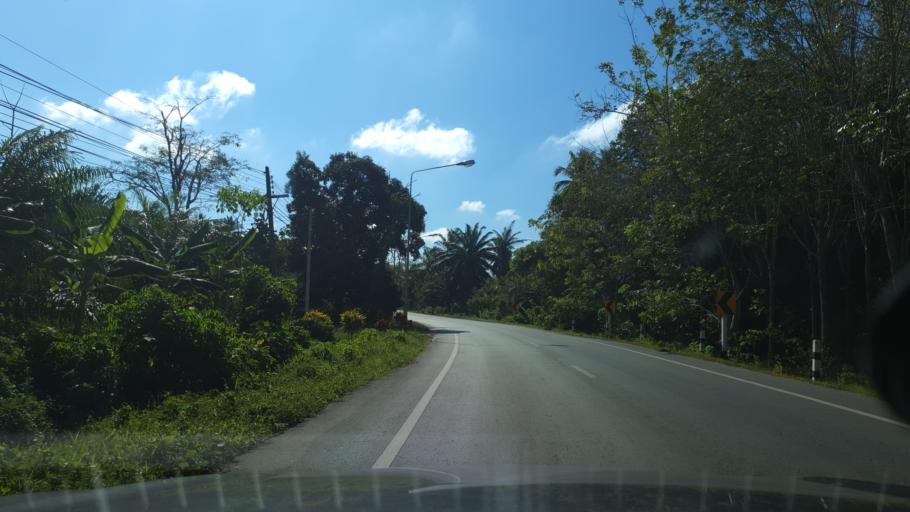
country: TH
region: Phangnga
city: Ban Ao Nang
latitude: 8.0722
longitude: 98.8072
